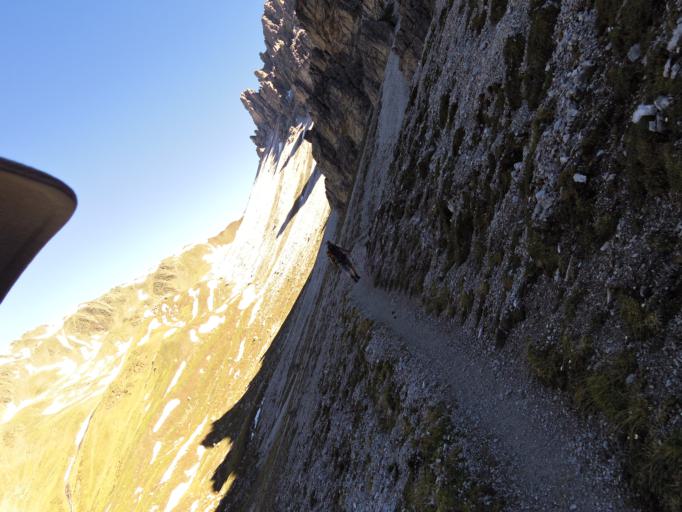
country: AT
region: Tyrol
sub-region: Politischer Bezirk Innsbruck Land
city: Neustift im Stubaital
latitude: 47.1370
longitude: 11.2761
